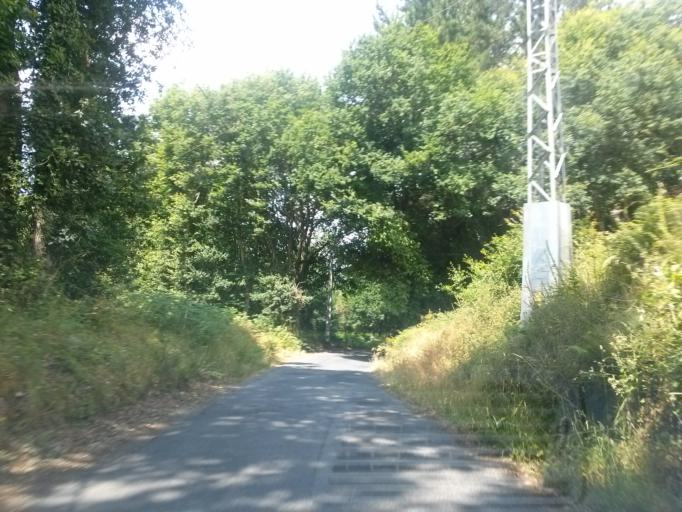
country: ES
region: Galicia
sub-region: Provincia de Lugo
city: Lugo
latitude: 43.0271
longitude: -7.5828
